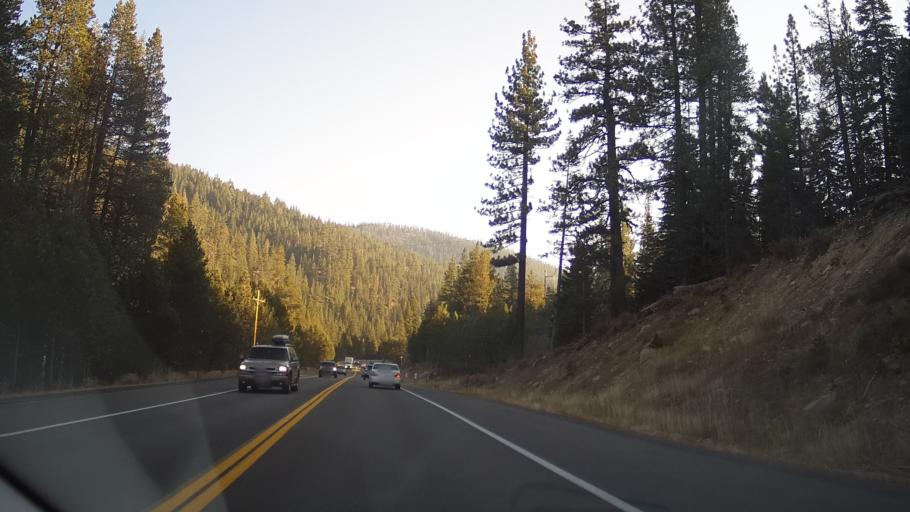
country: US
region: California
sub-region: Placer County
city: Sunnyside-Tahoe City
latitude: 39.2138
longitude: -120.2013
